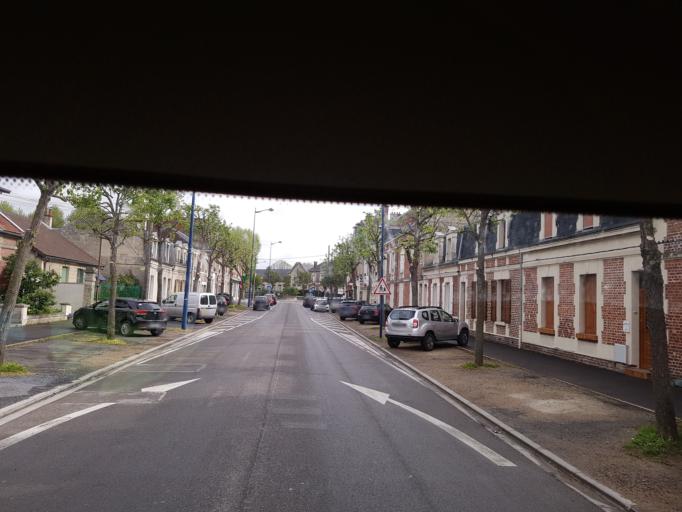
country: FR
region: Picardie
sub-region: Departement de l'Aisne
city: Soissons
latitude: 49.3818
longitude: 3.3349
